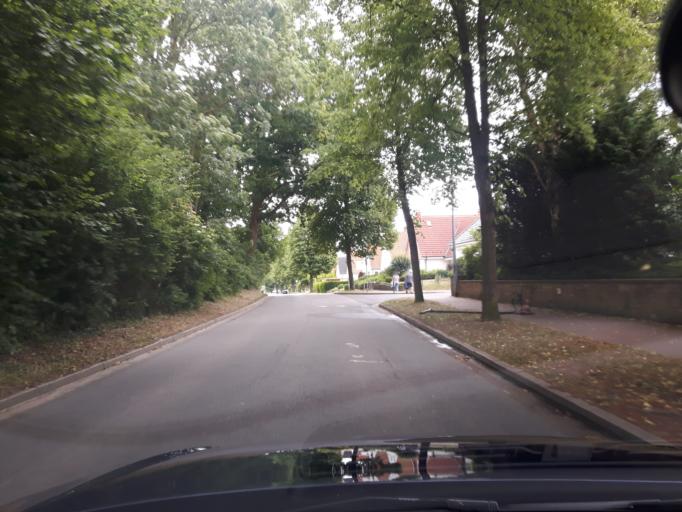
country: DE
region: Schleswig-Holstein
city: Neustadt in Holstein
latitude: 54.0949
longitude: 10.8550
